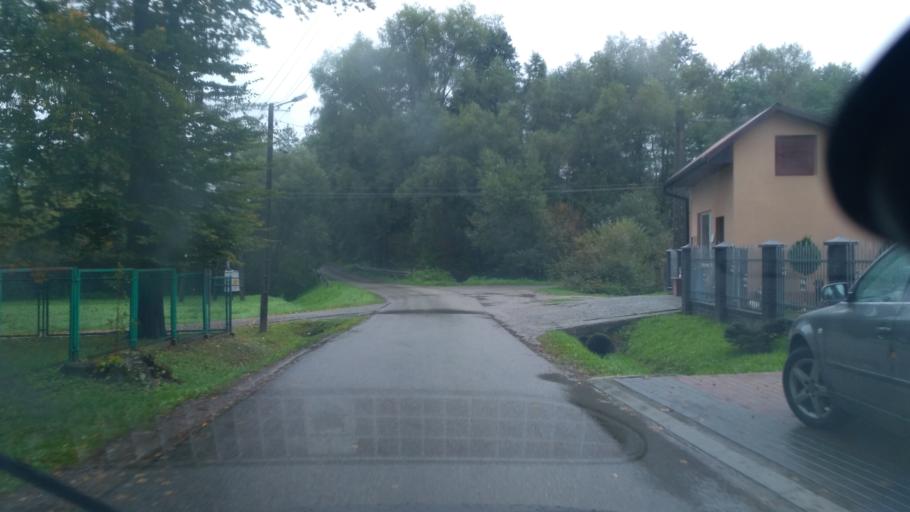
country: PL
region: Subcarpathian Voivodeship
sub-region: Powiat ropczycko-sedziszowski
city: Niedzwiada
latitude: 50.0219
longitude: 21.5405
